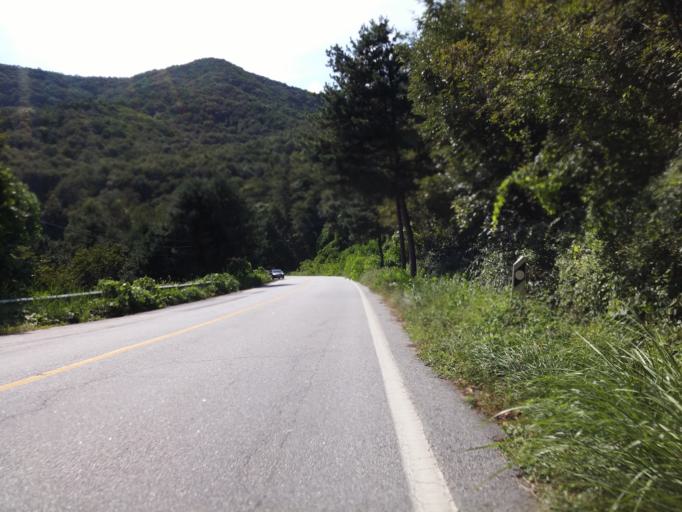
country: KR
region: Daejeon
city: Sintansin
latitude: 36.4874
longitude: 127.4866
